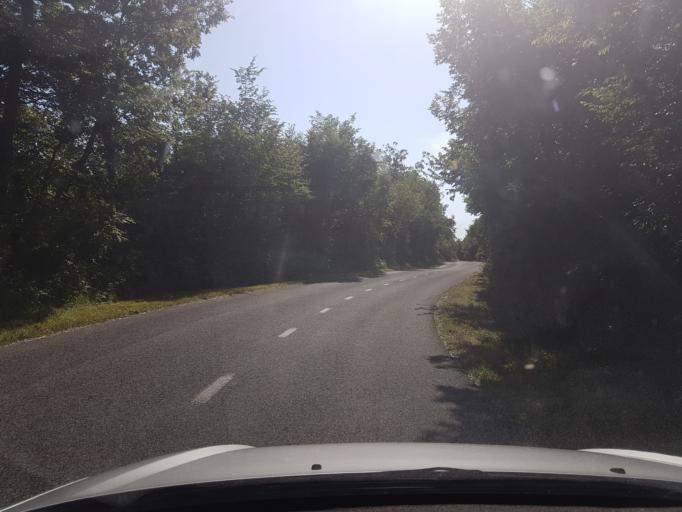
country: SI
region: Vipava
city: Vipava
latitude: 45.7688
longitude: 13.9384
